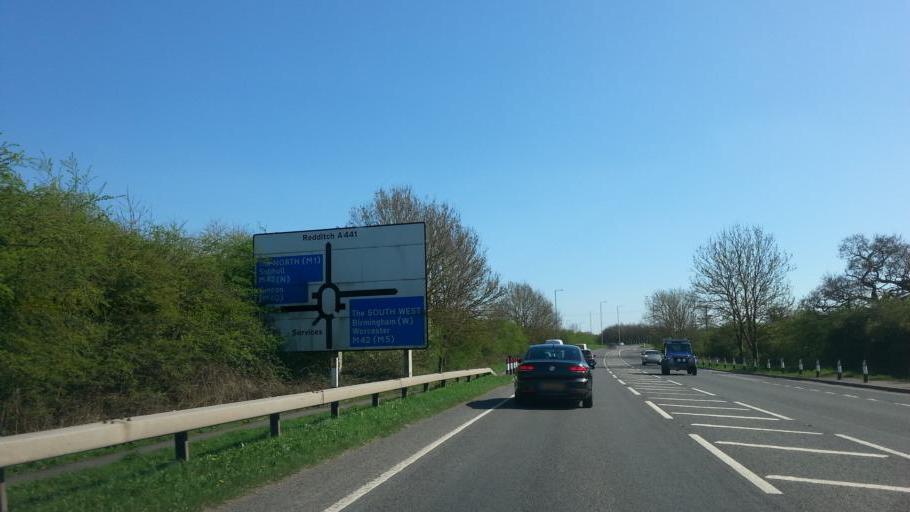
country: GB
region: England
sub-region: Worcestershire
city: Alvechurch
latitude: 52.3649
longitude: -1.9508
